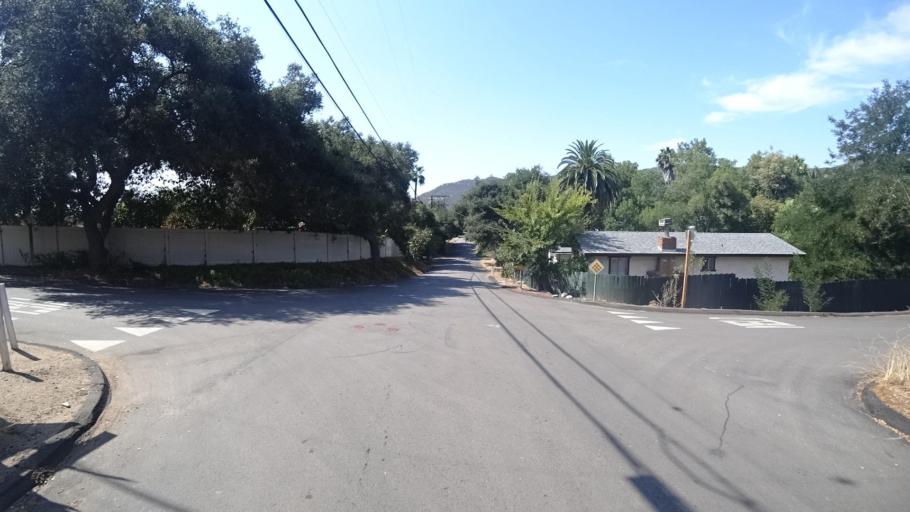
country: US
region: California
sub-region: San Diego County
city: Hidden Meadows
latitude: 33.1798
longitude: -117.1098
